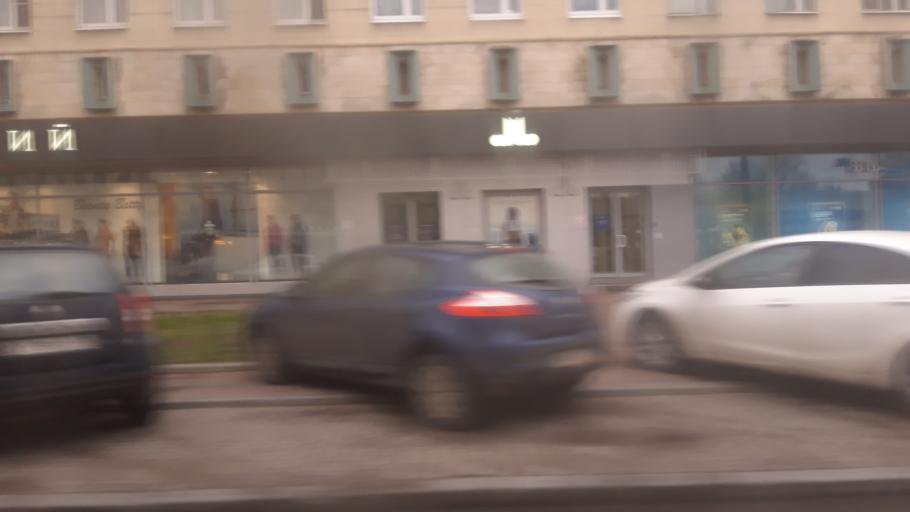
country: RU
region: St.-Petersburg
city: Kupchino
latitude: 59.8458
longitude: 30.3220
